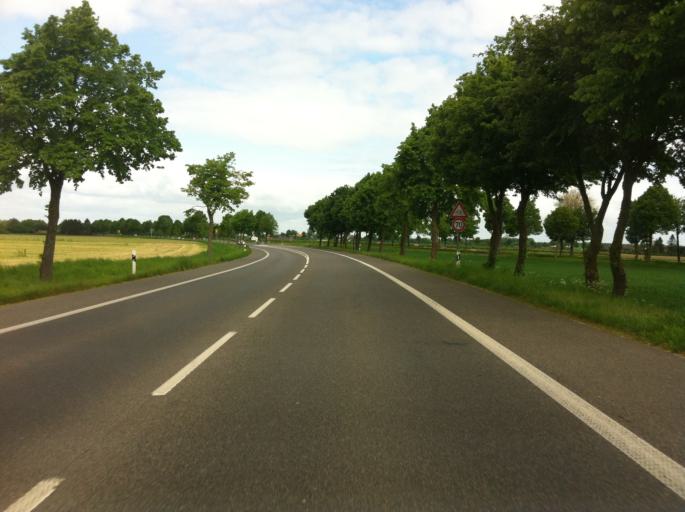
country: DE
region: North Rhine-Westphalia
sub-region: Regierungsbezirk Dusseldorf
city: Niederkruchten
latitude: 51.2189
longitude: 6.2077
